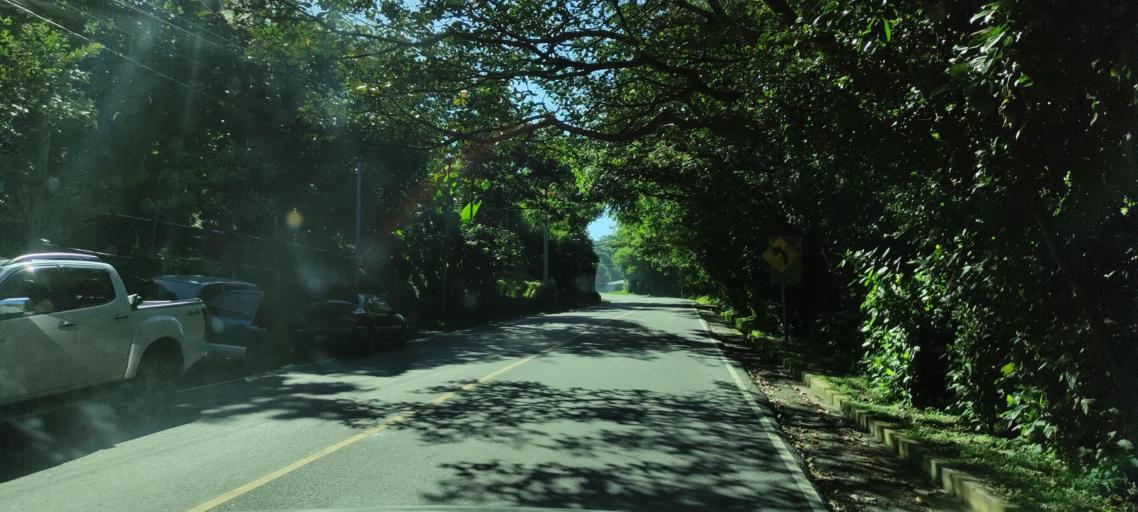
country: HN
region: Ocotepeque
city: Antigua Ocotepeque
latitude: 14.3195
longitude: -89.1755
